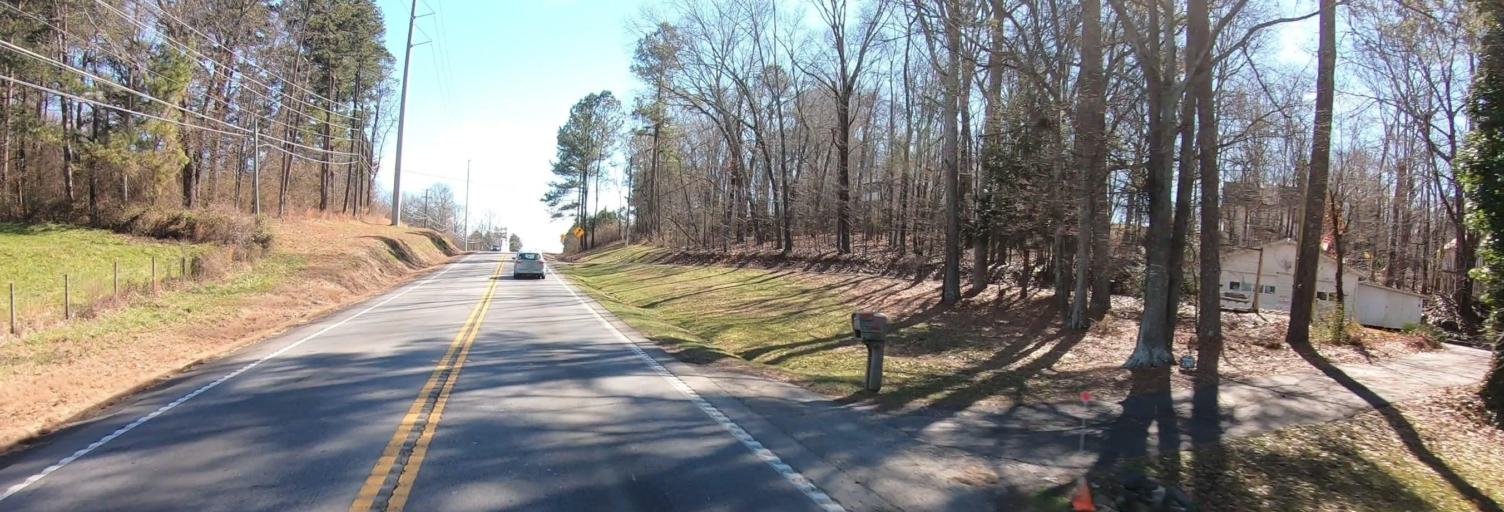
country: US
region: Georgia
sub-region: Forsyth County
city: Cumming
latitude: 34.2840
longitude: -84.1325
